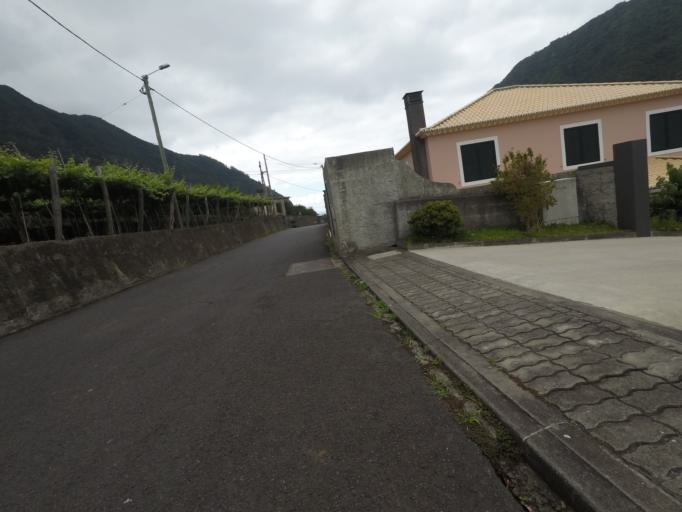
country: PT
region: Madeira
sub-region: Sao Vicente
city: Sao Vicente
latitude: 32.7915
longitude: -17.0395
